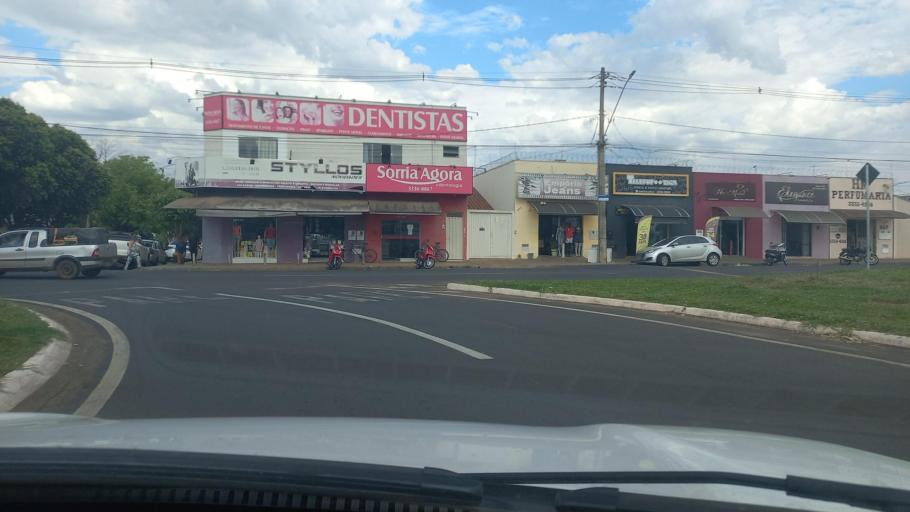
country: BR
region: Minas Gerais
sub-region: Uberaba
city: Uberaba
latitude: -19.7586
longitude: -47.9894
